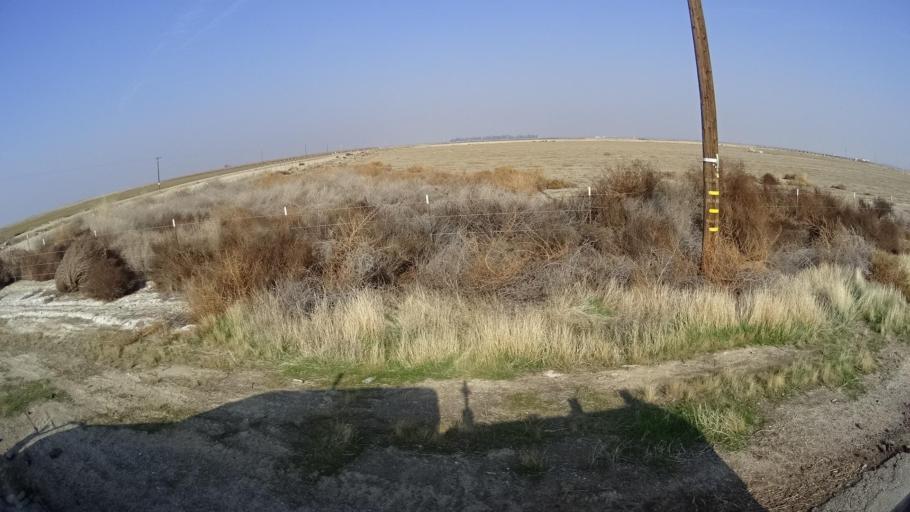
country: US
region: California
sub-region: Kern County
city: Buttonwillow
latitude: 35.3331
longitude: -119.3711
